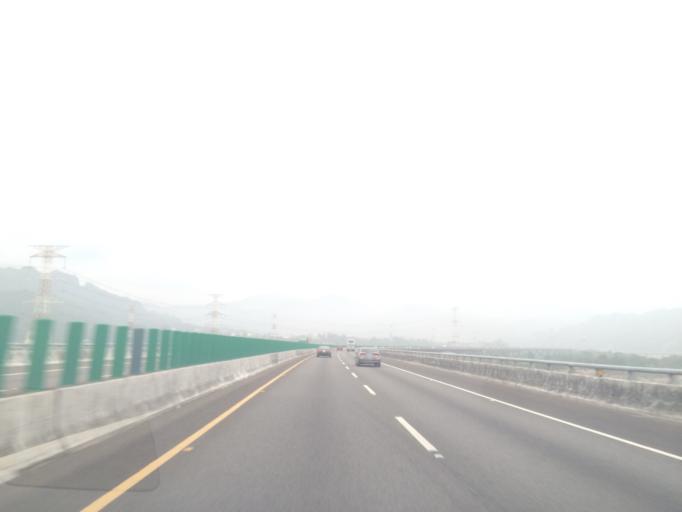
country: TW
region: Taiwan
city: Zhongxing New Village
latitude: 23.9956
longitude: 120.7463
